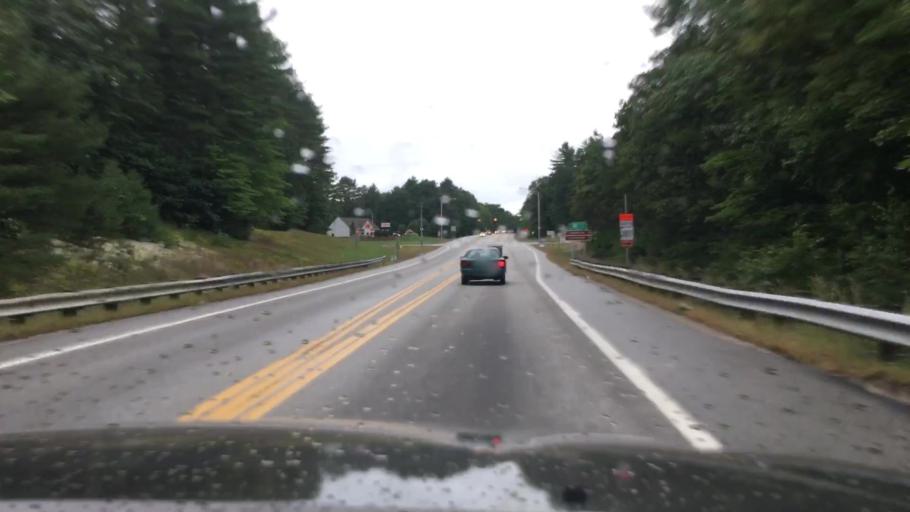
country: US
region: New Hampshire
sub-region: Merrimack County
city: Contoocook
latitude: 43.1788
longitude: -71.7525
